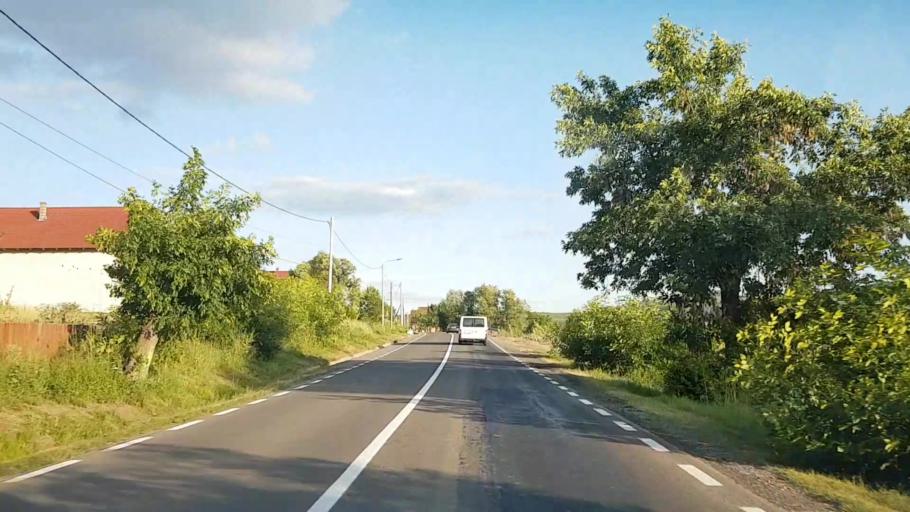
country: RO
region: Harghita
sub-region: Comuna Corund
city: Corund
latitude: 46.4814
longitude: 25.1722
